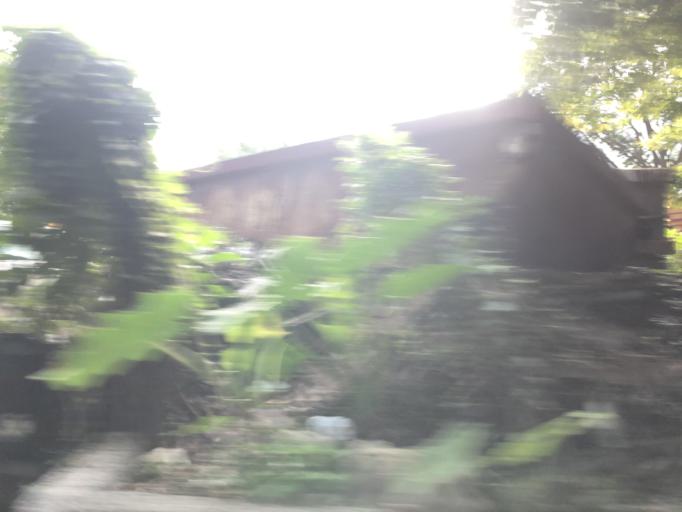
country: TW
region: Taiwan
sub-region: Keelung
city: Keelung
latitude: 25.1910
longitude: 121.6435
